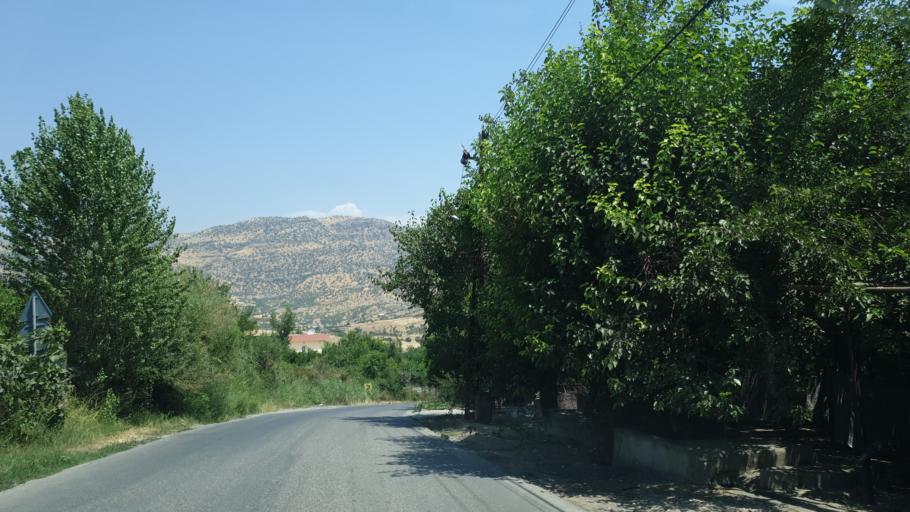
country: IQ
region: Arbil
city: Nahiyat Hiran
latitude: 36.2817
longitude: 44.5004
